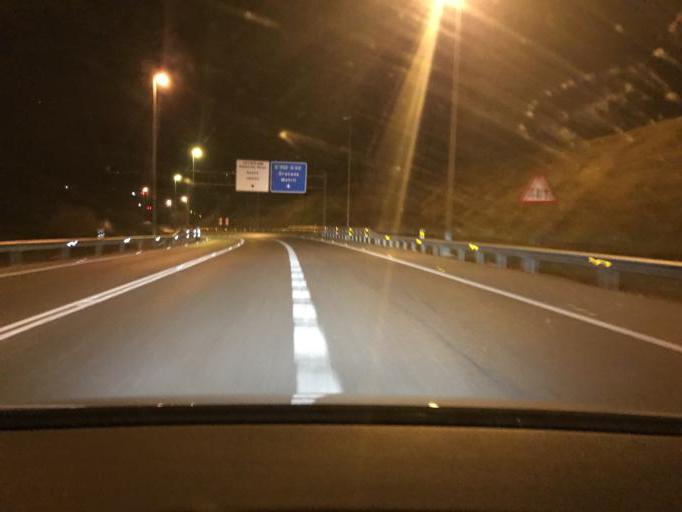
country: ES
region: Andalusia
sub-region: Provincia de Jaen
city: Jaen
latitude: 37.7798
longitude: -3.7521
